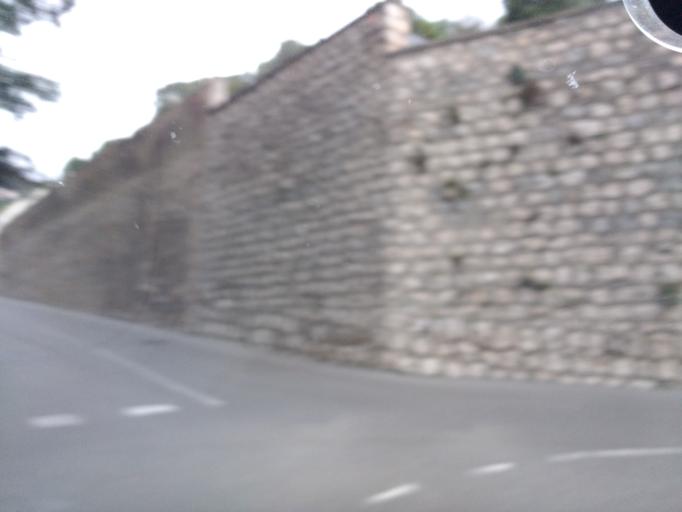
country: FR
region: Provence-Alpes-Cote d'Azur
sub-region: Departement des Alpes-Maritimes
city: Beaulieu-sur-Mer
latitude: 43.7085
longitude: 7.3265
